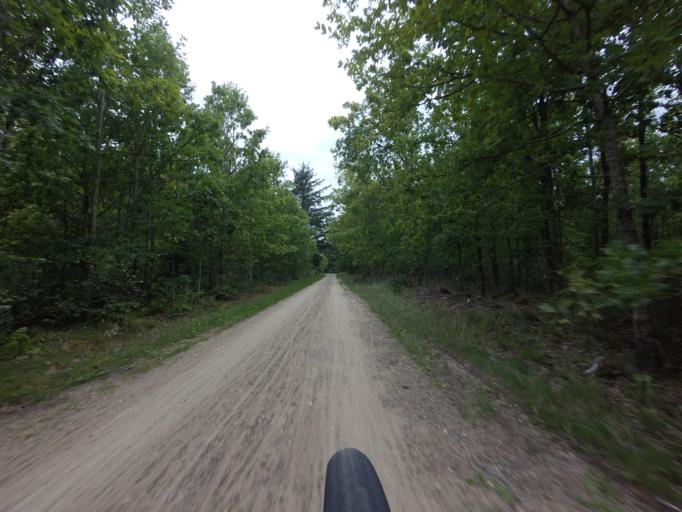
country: DK
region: North Denmark
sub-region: Hjorring Kommune
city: Hirtshals
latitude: 57.5838
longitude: 10.0560
